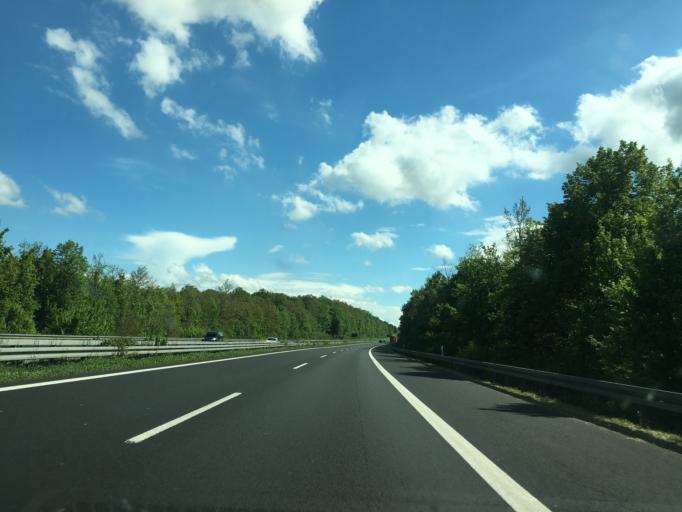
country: DE
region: Bavaria
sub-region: Regierungsbezirk Unterfranken
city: Rottendorf
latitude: 49.8232
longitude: 10.0431
